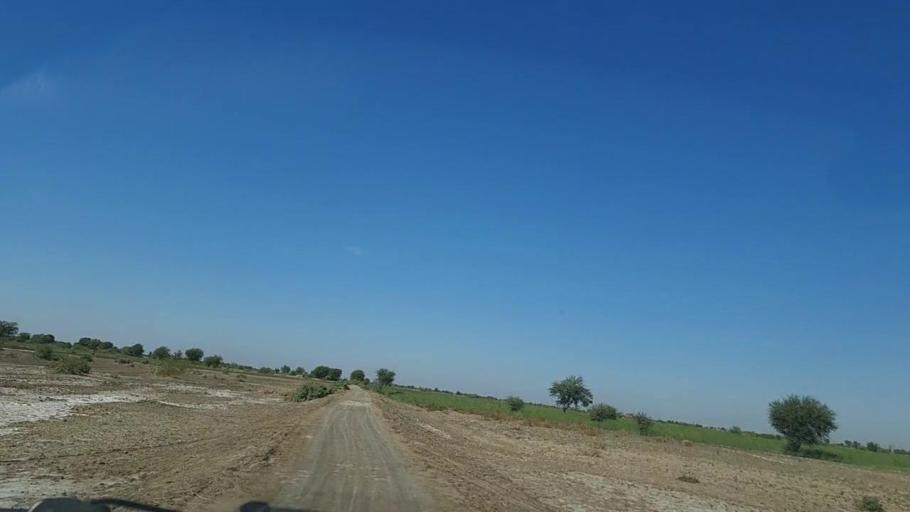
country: PK
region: Sindh
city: Pithoro
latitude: 25.5585
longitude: 69.4603
